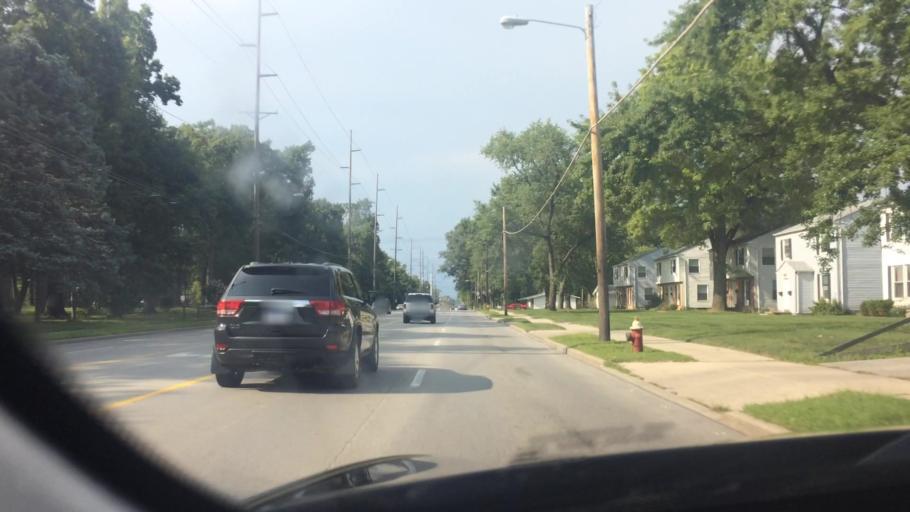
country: US
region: Ohio
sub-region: Lucas County
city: Ottawa Hills
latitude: 41.7007
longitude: -83.6234
